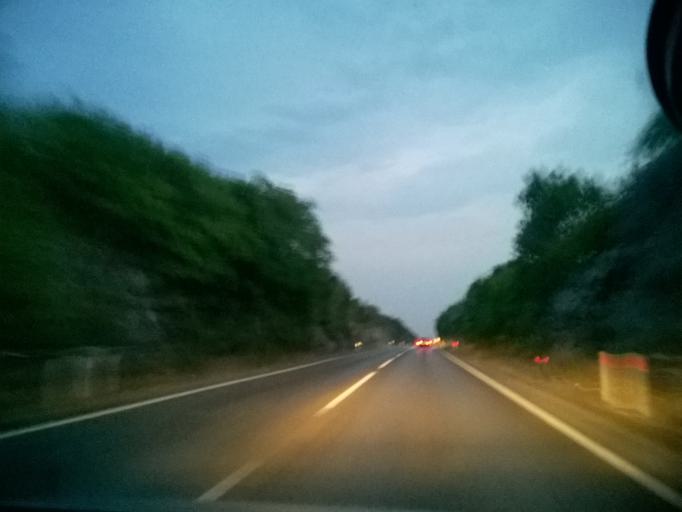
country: ME
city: Spuz
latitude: 42.4960
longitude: 19.1536
